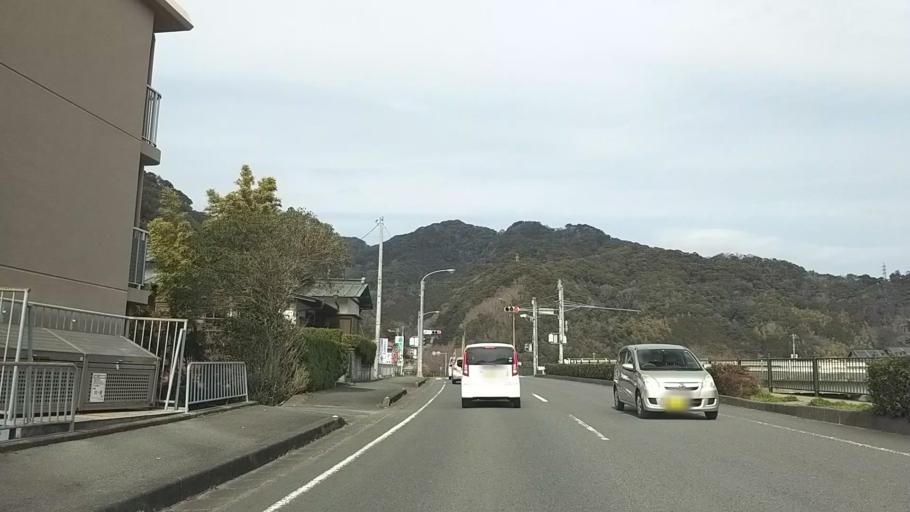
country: JP
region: Shizuoka
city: Shimoda
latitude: 34.7023
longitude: 138.9405
